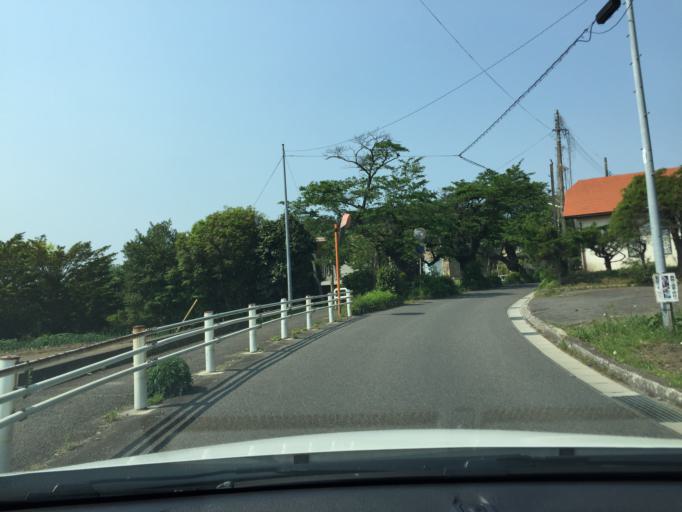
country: JP
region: Tochigi
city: Kuroiso
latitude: 37.1168
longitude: 140.2096
